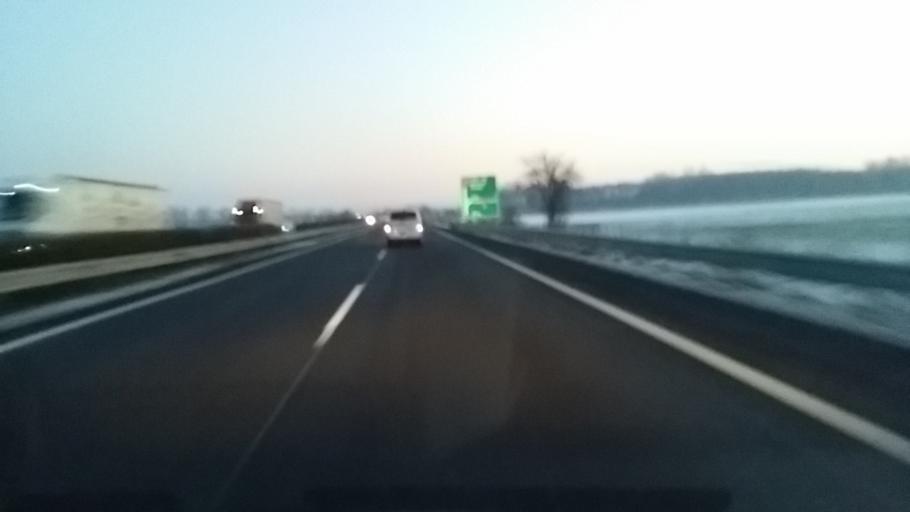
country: CZ
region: South Moravian
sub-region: Okres Breclav
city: Lanzhot
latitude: 48.6494
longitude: 16.9955
